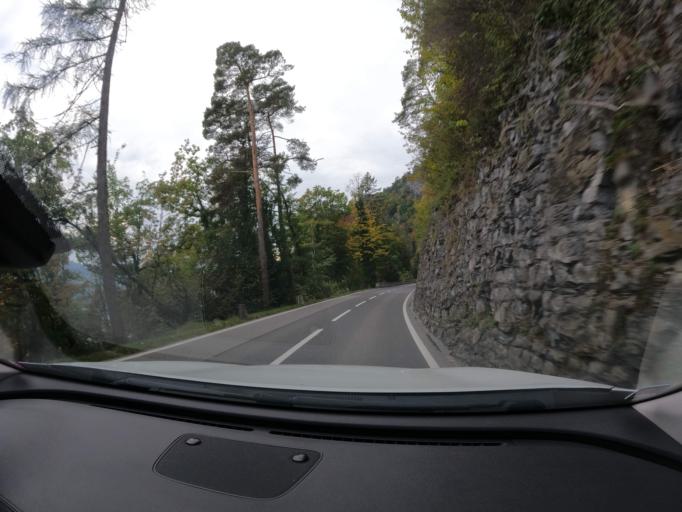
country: CH
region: Bern
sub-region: Interlaken-Oberhasli District
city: Beatenberg
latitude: 46.6828
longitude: 7.7671
